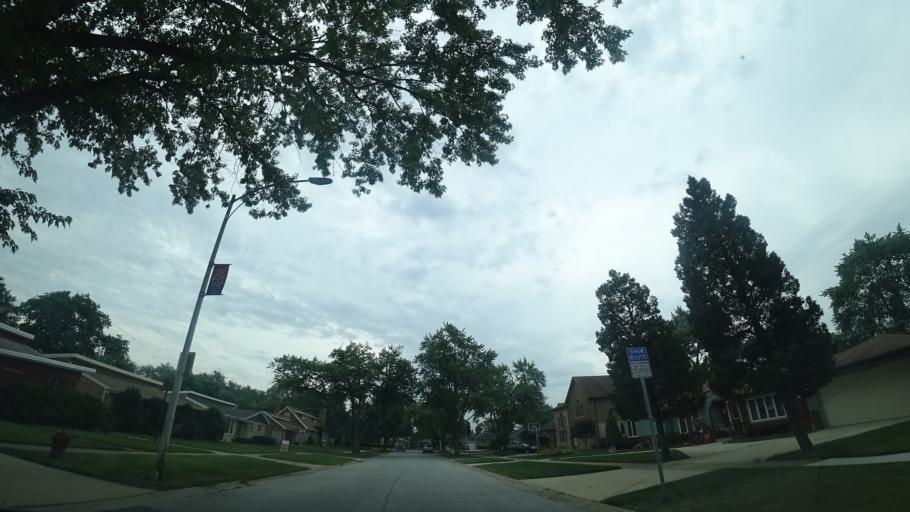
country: US
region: Illinois
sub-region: Cook County
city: Merrionette Park
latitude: 41.6995
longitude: -87.7255
